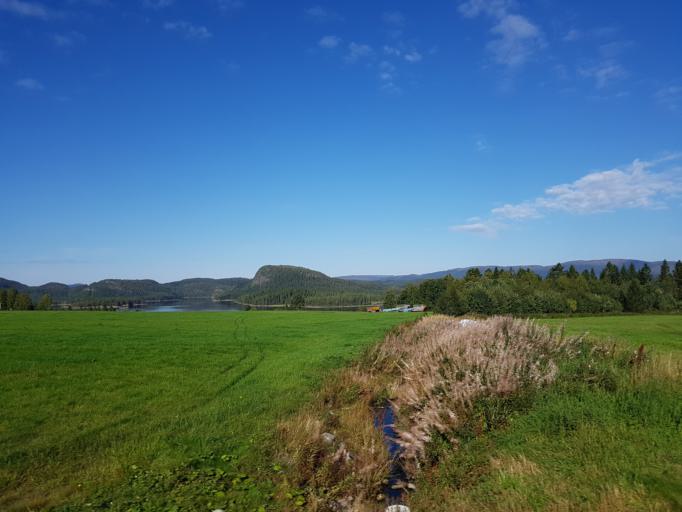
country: NO
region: Sor-Trondelag
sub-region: Trondheim
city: Trondheim
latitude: 63.5956
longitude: 10.2166
